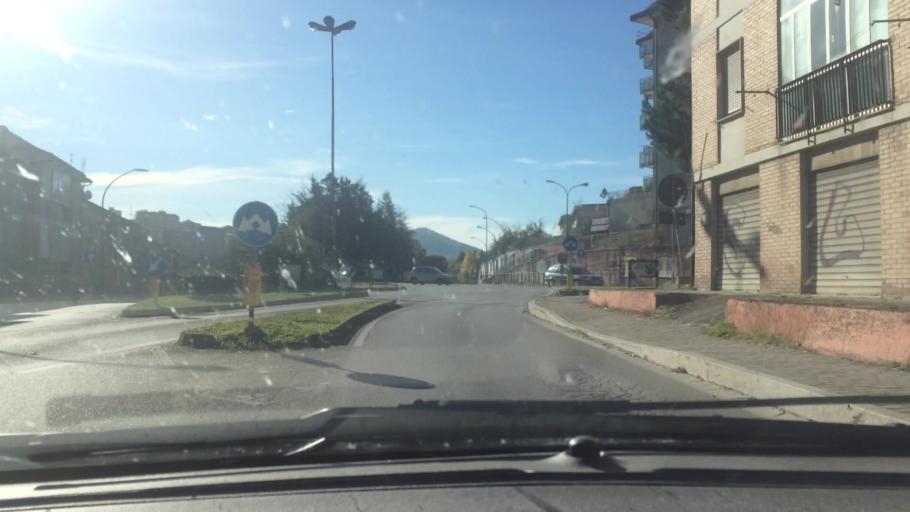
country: IT
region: Basilicate
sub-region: Provincia di Potenza
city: Potenza
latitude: 40.6477
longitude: 15.7947
